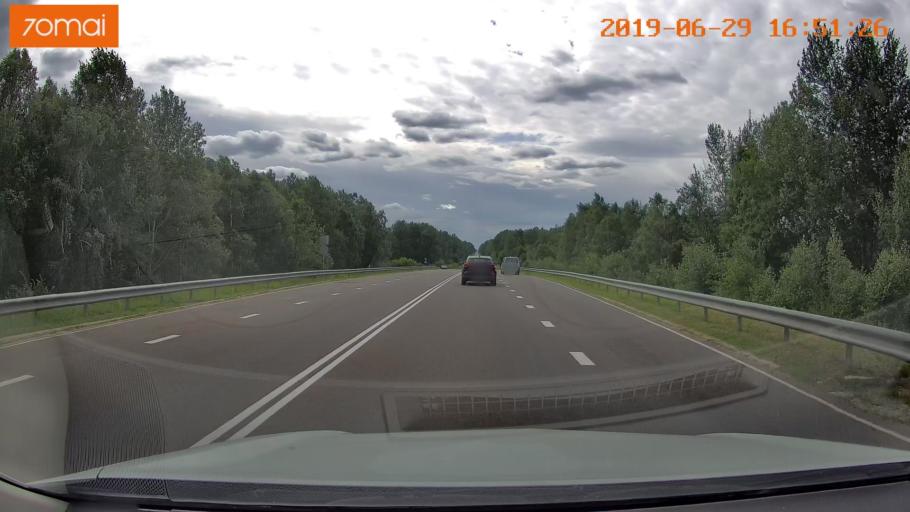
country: BY
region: Brest
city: Luninyets
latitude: 52.2809
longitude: 26.8249
